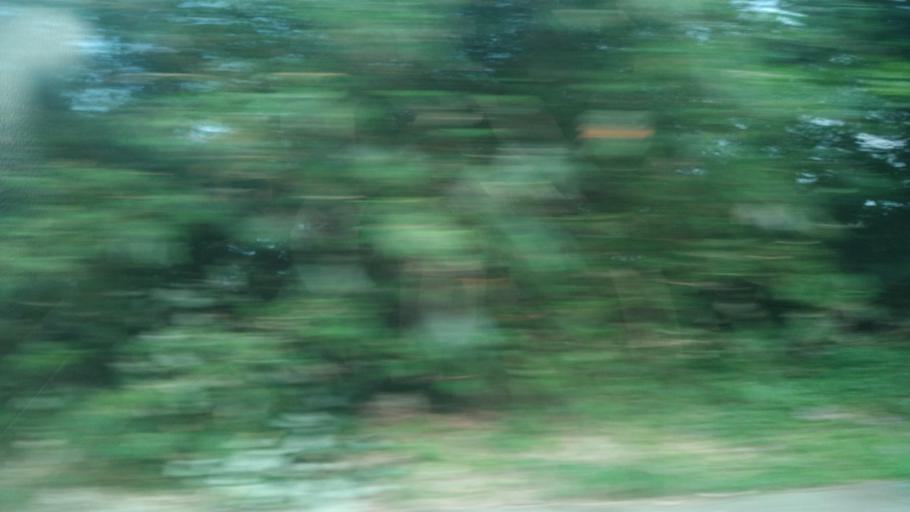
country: TW
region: Taiwan
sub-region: Keelung
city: Keelung
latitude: 25.2368
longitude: 121.6297
